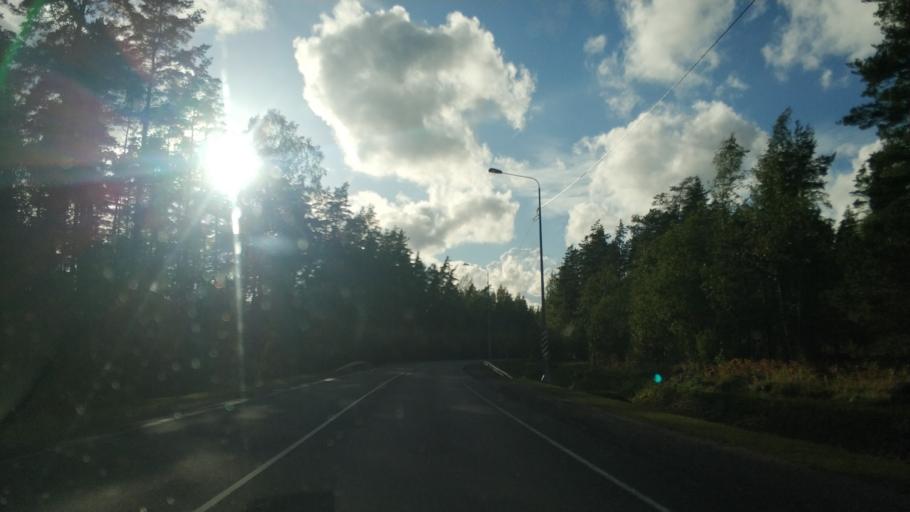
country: RU
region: Leningrad
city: Sapernoye
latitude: 60.7136
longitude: 30.0194
